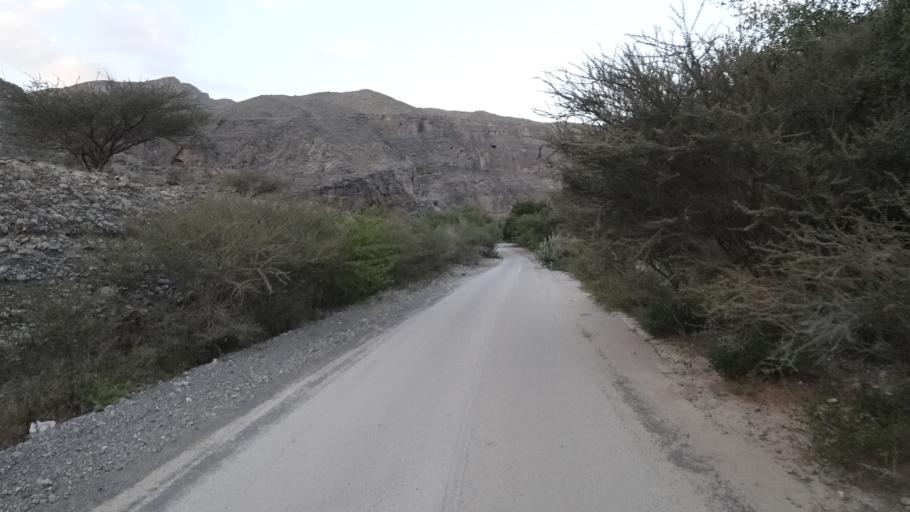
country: OM
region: Muhafazat ad Dakhiliyah
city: Nizwa
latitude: 23.0641
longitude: 57.4691
